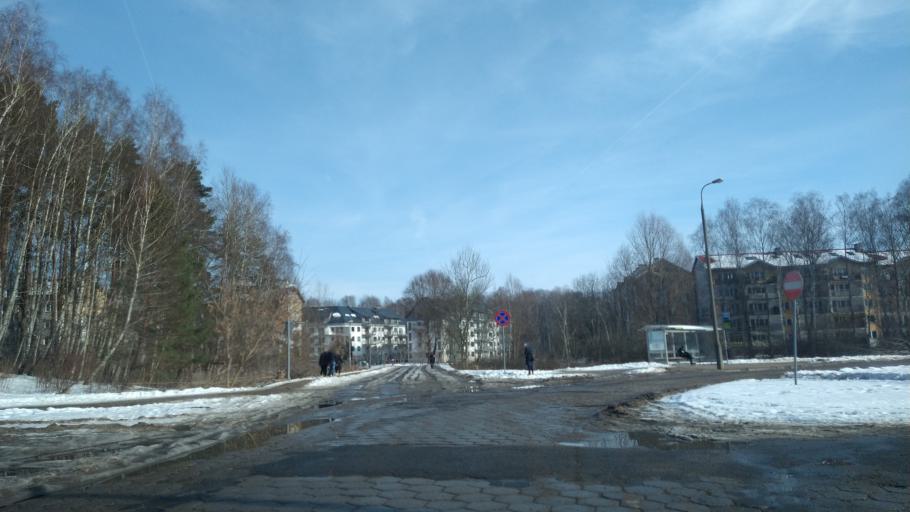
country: PL
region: Warmian-Masurian Voivodeship
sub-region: Powiat olsztynski
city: Olsztyn
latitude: 53.7402
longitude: 20.5174
